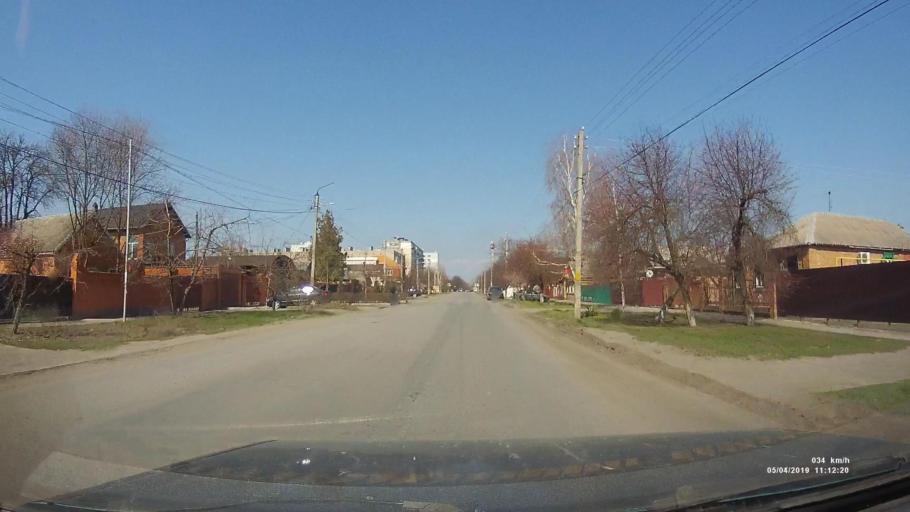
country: RU
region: Rostov
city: Azov
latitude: 47.0976
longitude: 39.4379
